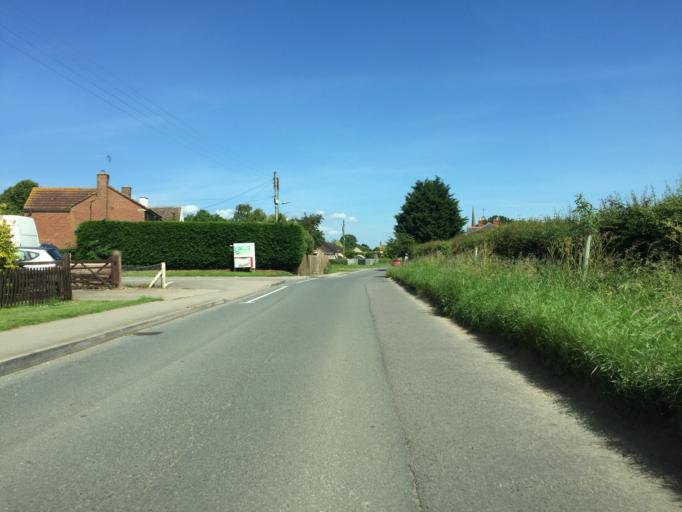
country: GB
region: England
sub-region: Gloucestershire
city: Dursley
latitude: 51.7257
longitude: -2.3756
